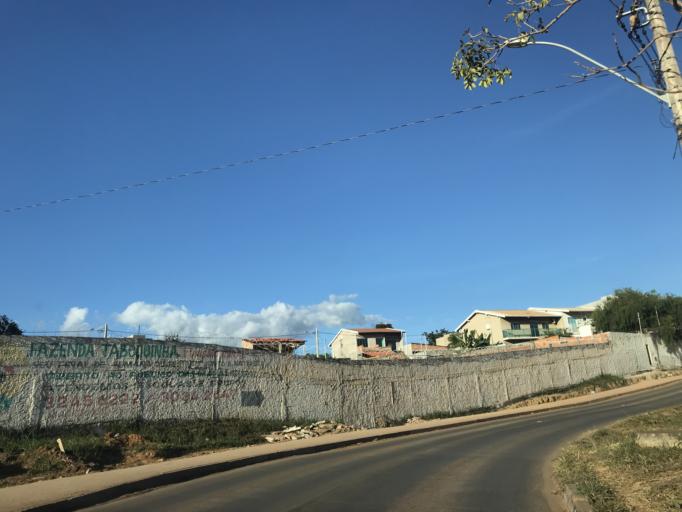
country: BR
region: Federal District
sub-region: Brasilia
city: Brasilia
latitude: -15.8827
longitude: -47.7677
